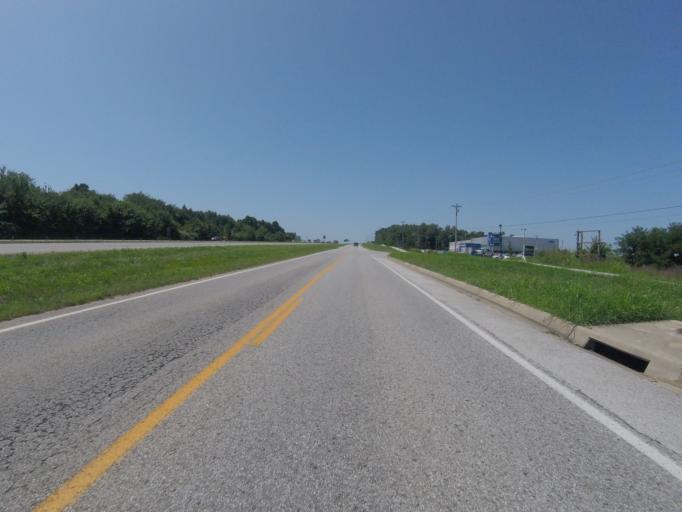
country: US
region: Arkansas
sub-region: Washington County
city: Johnson
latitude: 36.1020
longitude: -94.1839
